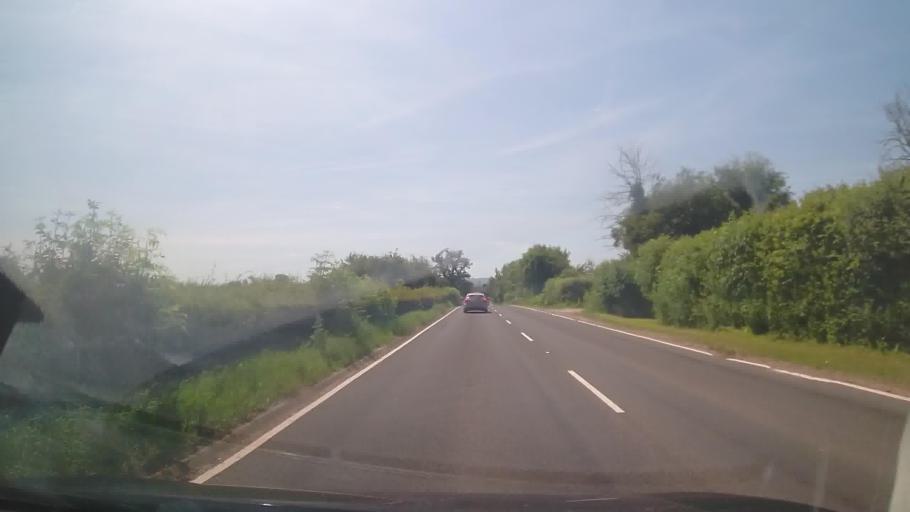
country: GB
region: England
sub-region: Herefordshire
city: Hereford
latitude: 52.0835
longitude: -2.7223
